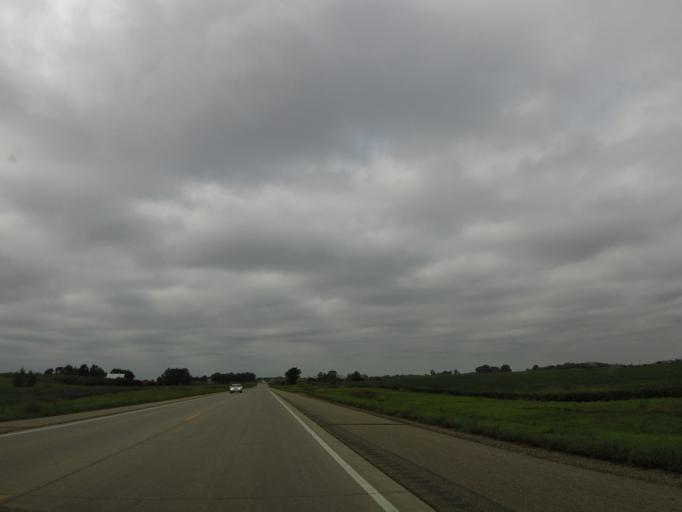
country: US
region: Minnesota
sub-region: Renville County
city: Renville
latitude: 44.7890
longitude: -95.1092
